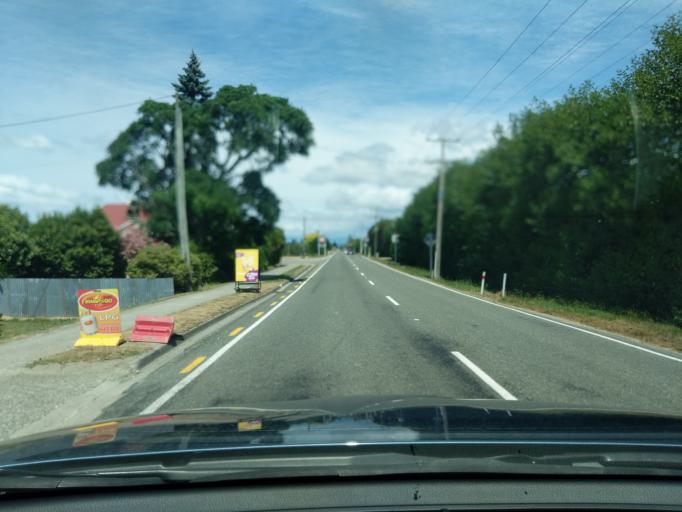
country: NZ
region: Tasman
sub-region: Tasman District
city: Motueka
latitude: -41.0853
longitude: 172.9970
